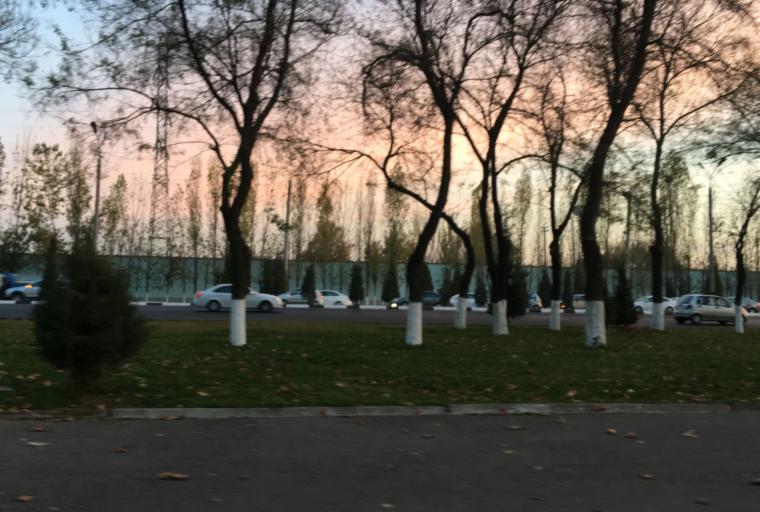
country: UZ
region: Toshkent
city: Salor
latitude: 41.3230
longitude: 69.3639
